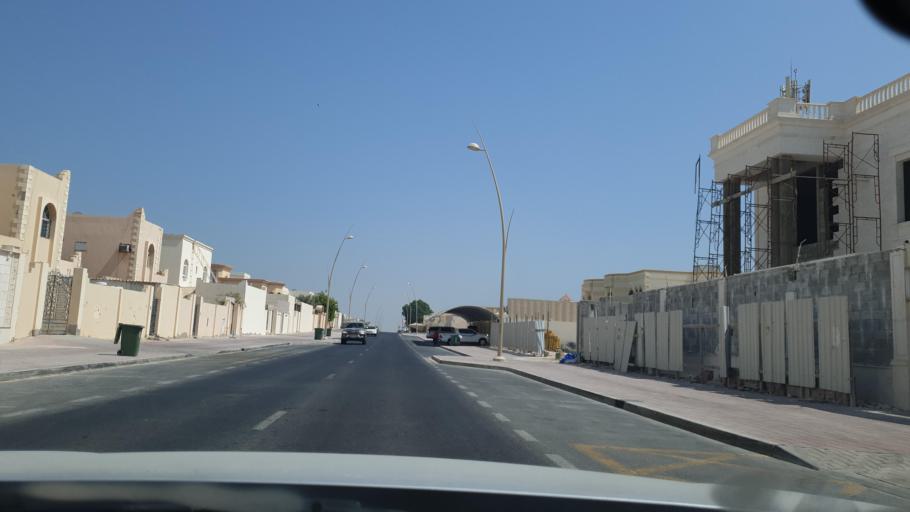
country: QA
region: Al Khawr
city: Al Khawr
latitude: 25.6827
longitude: 51.5200
